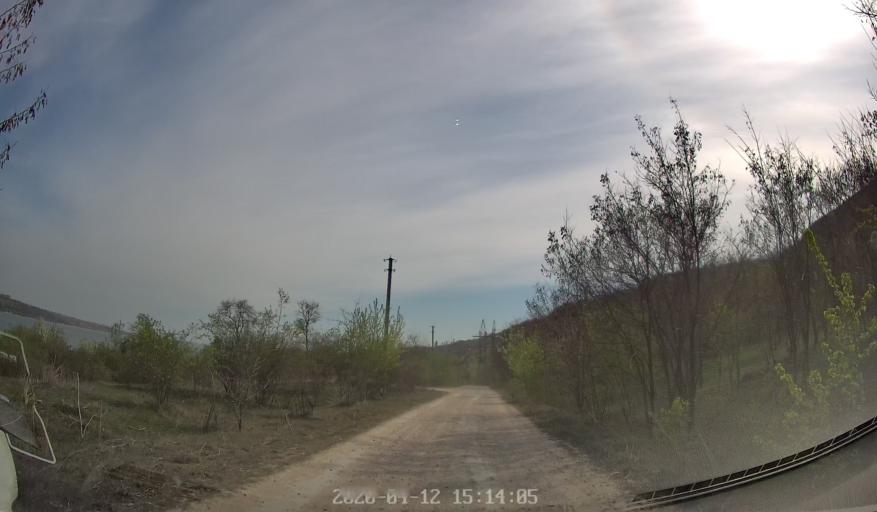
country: MD
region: Telenesti
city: Cocieri
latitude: 47.3255
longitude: 29.0739
